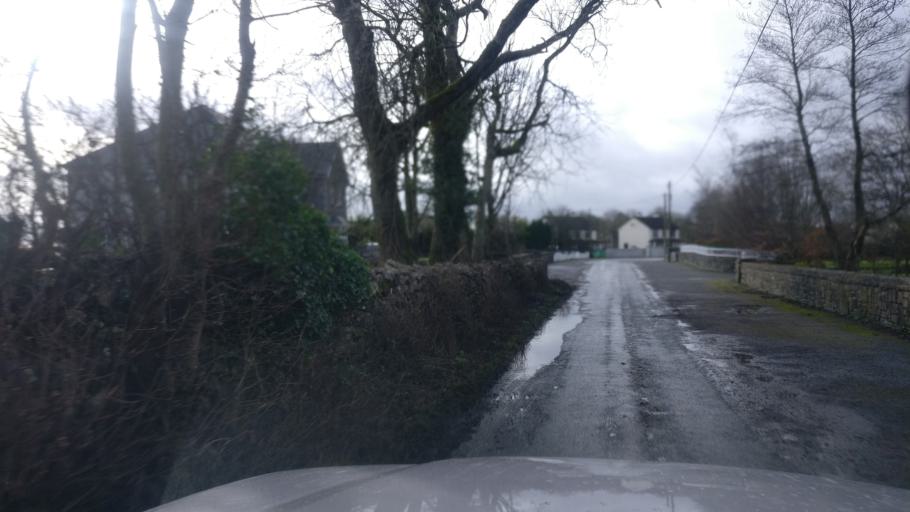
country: IE
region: Connaught
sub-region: County Galway
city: Athenry
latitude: 53.2639
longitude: -8.7935
